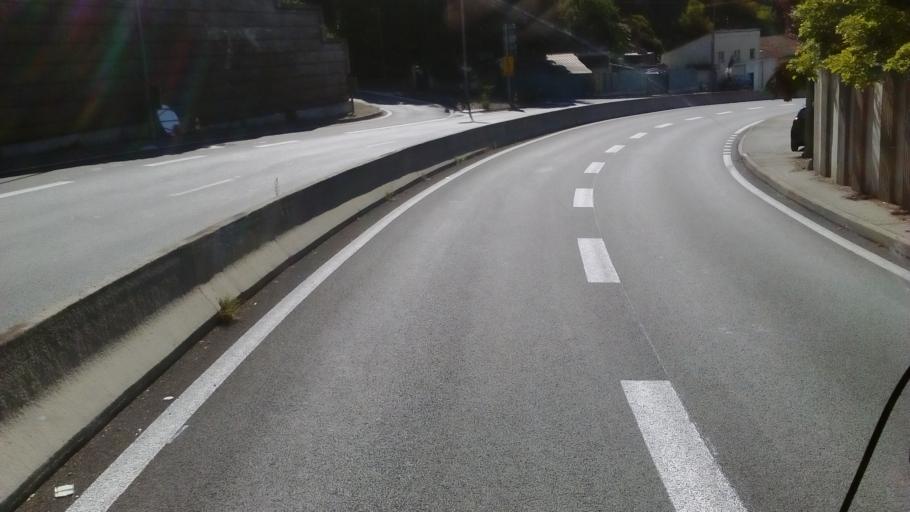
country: FR
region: Provence-Alpes-Cote d'Azur
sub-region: Departement des Alpes-Maritimes
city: La Turbie
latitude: 43.7328
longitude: 7.3902
